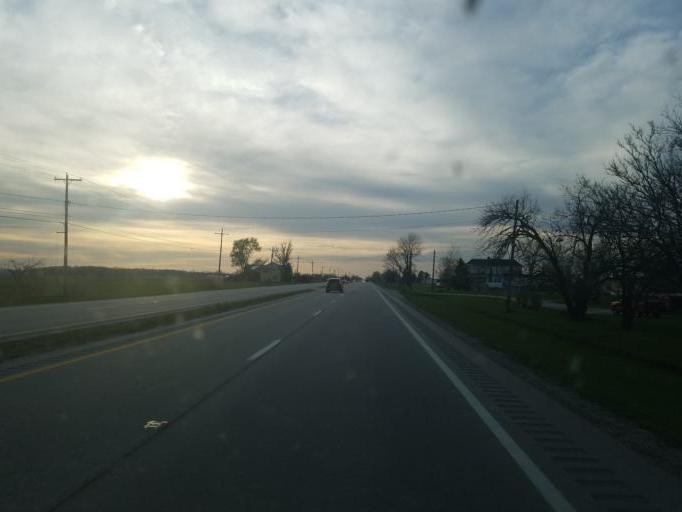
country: US
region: Ohio
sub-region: Sandusky County
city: Gibsonburg
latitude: 41.4110
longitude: -83.2655
